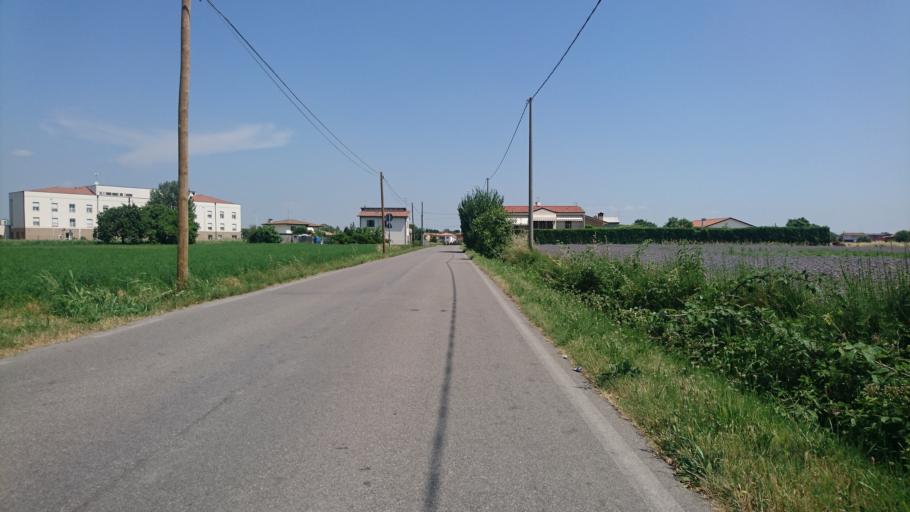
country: IT
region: Veneto
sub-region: Provincia di Padova
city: Solesino
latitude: 45.1699
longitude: 11.7387
